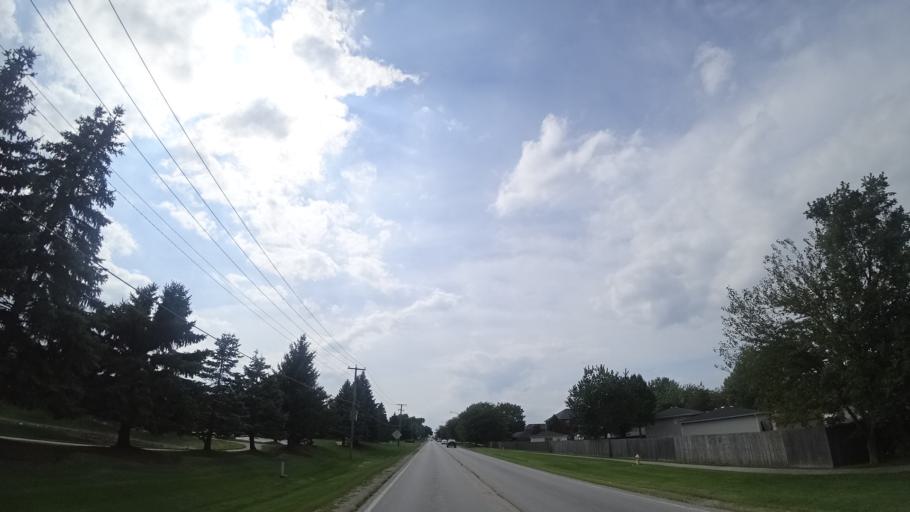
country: US
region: Illinois
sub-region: Cook County
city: Tinley Park
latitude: 41.5588
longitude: -87.7764
